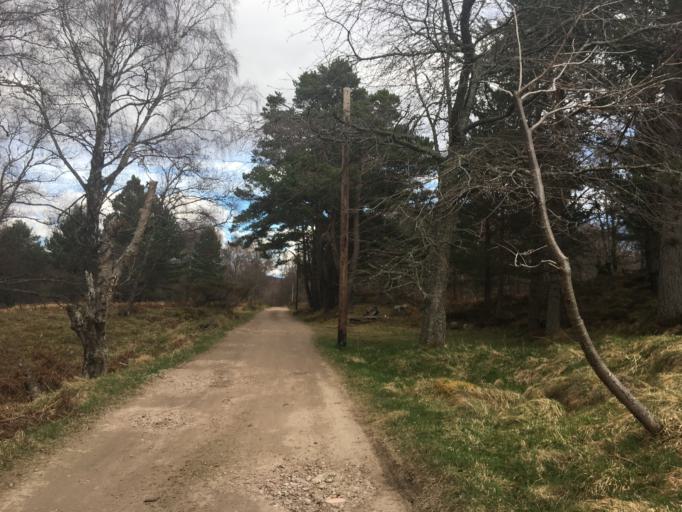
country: GB
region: Scotland
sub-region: Highland
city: Aviemore
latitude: 57.1629
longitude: -3.8142
